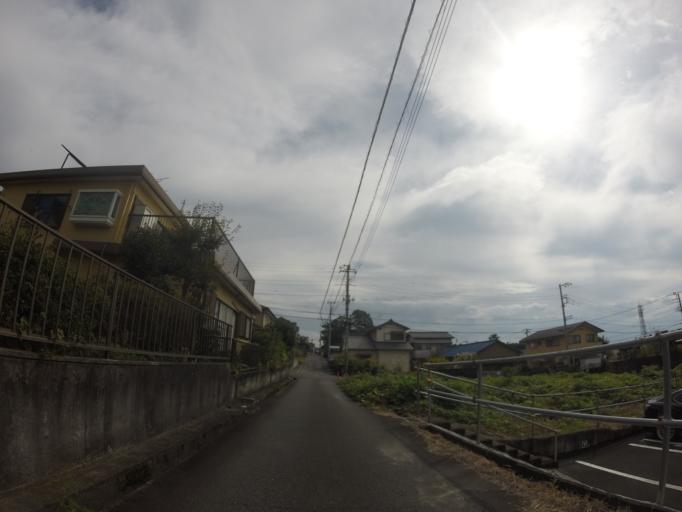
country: JP
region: Shizuoka
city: Fuji
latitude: 35.2207
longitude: 138.6822
